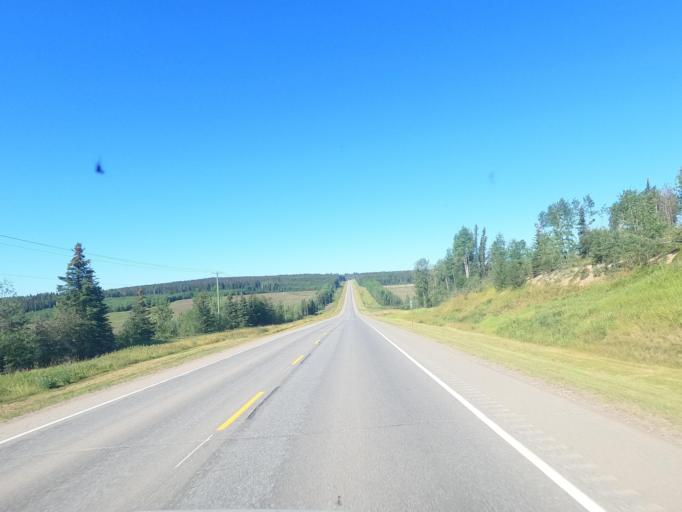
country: CA
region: British Columbia
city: Fort St. John
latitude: 56.6296
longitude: -121.5372
